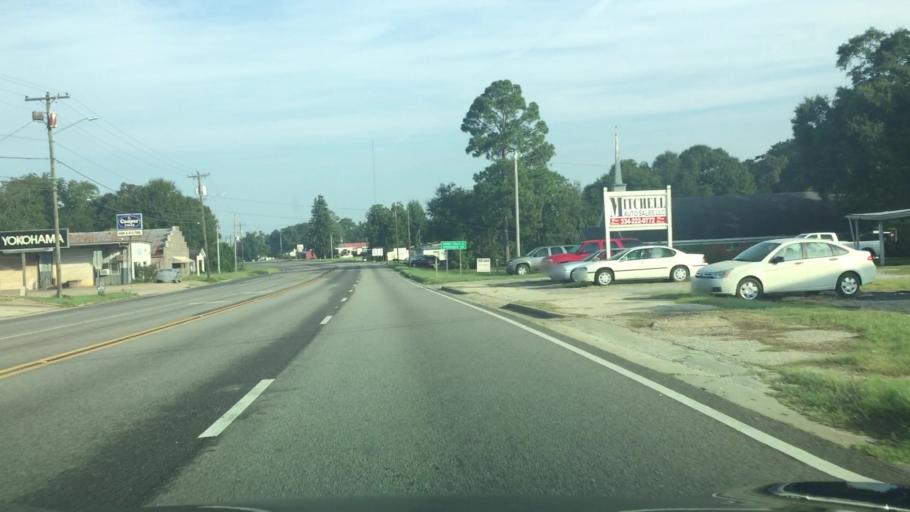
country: US
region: Alabama
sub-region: Covington County
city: Andalusia
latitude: 31.3192
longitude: -86.4990
